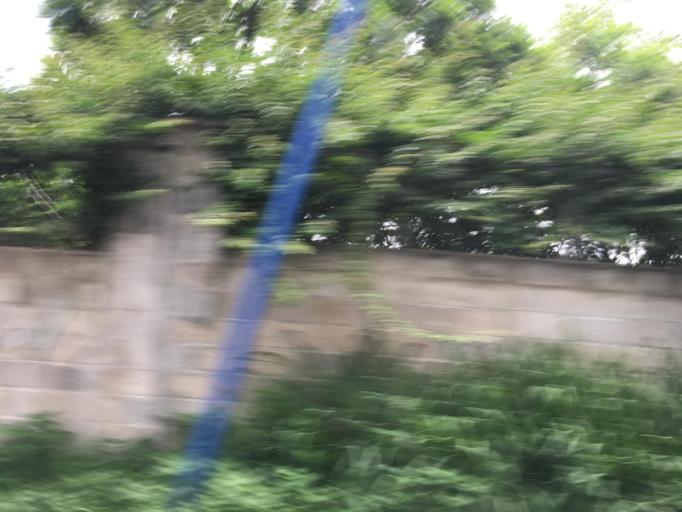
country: GT
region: Guatemala
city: Amatitlan
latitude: 14.4744
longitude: -90.5945
